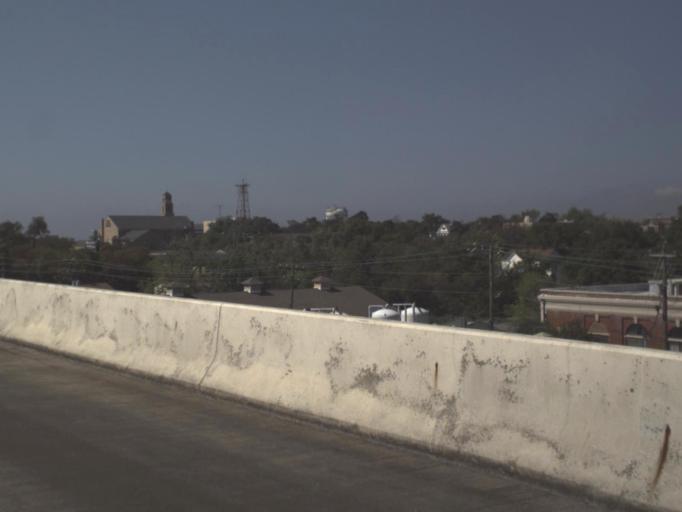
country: US
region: Florida
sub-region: Escambia County
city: Pensacola
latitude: 30.4241
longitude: -87.2148
